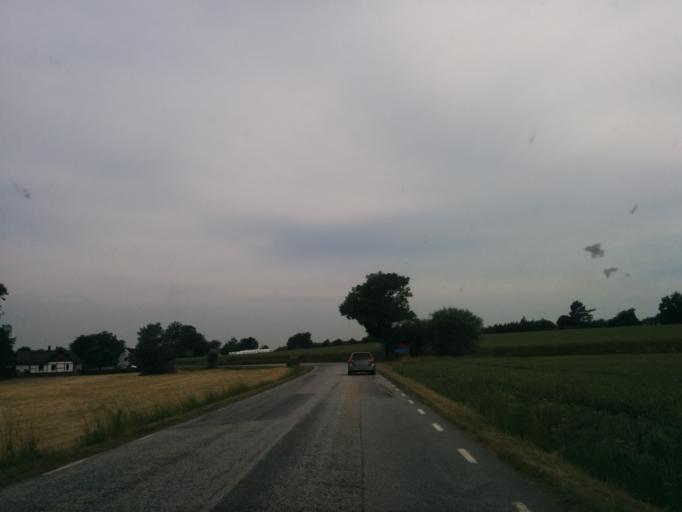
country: SE
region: Skane
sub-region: Lunds Kommun
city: Genarp
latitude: 55.6403
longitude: 13.3591
